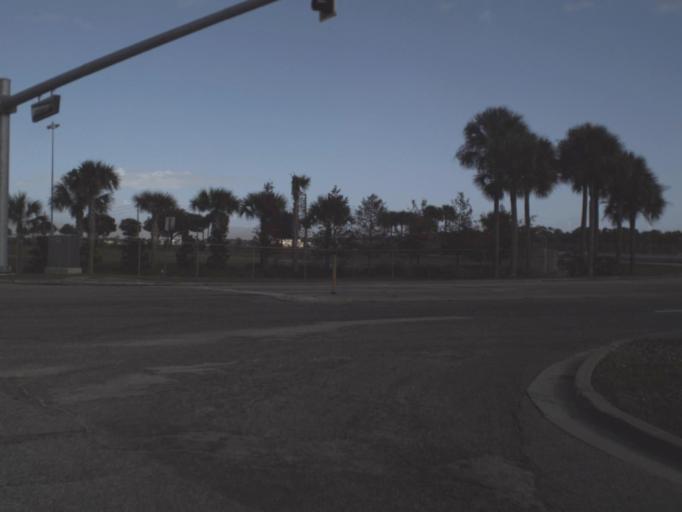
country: US
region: Florida
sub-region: Volusia County
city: Daytona Beach
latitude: 29.1751
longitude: -81.0785
